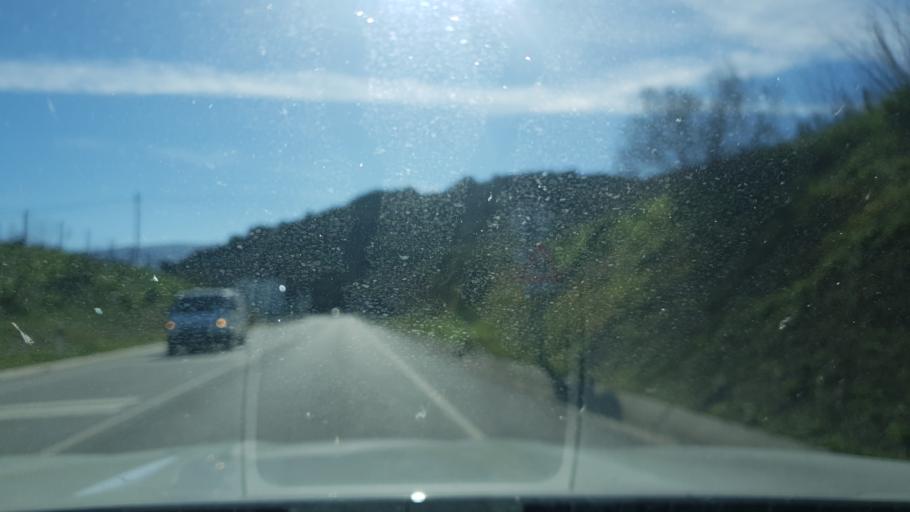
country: PT
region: Braganca
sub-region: Torre de Moncorvo
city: Torre de Moncorvo
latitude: 41.2130
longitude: -7.0889
